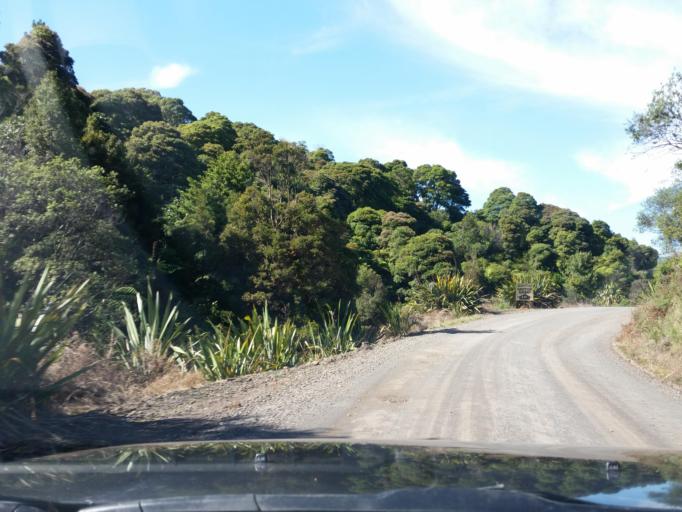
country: NZ
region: Northland
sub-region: Kaipara District
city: Dargaville
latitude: -35.7190
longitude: 173.6422
